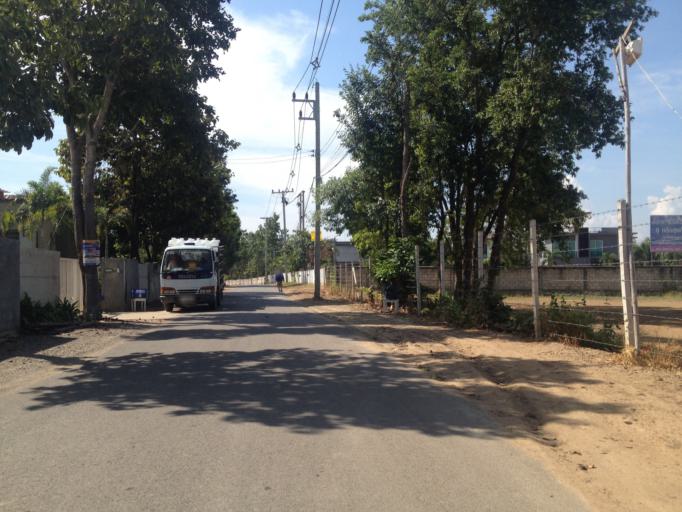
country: TH
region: Chiang Mai
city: Hang Dong
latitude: 18.7060
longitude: 98.9001
